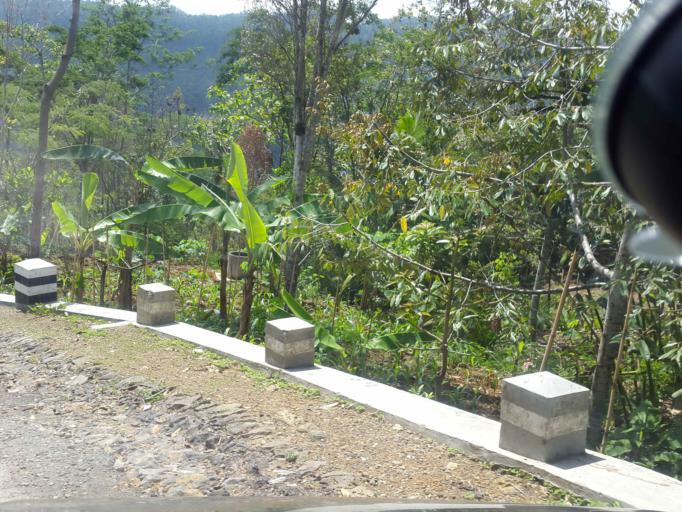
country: ID
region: East Java
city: Tawang
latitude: -8.1123
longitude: 111.5906
